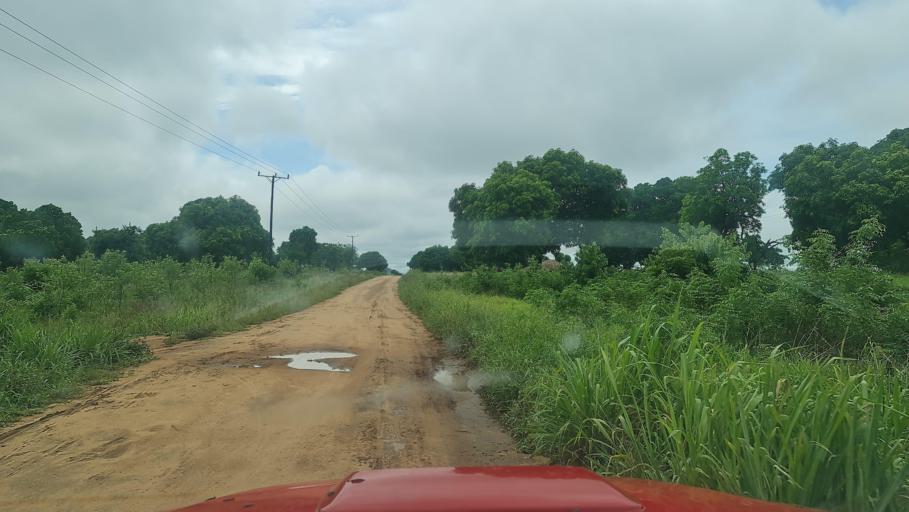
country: MW
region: Southern Region
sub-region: Nsanje District
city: Nsanje
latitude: -17.1814
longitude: 35.9125
